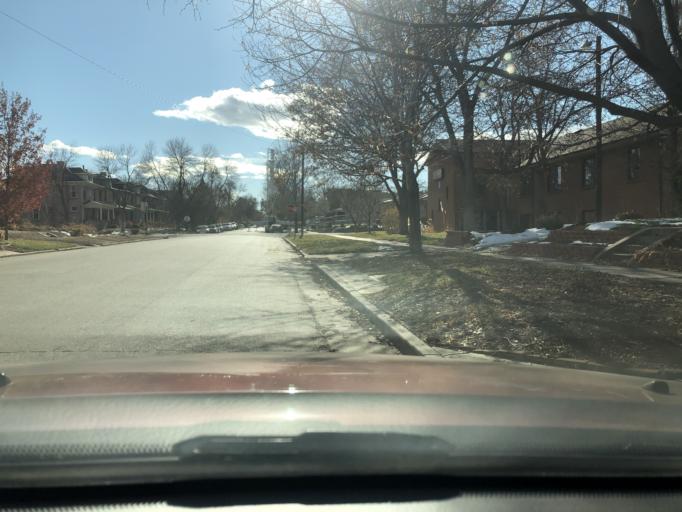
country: US
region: Colorado
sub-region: Denver County
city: Denver
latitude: 39.7501
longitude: -104.9611
